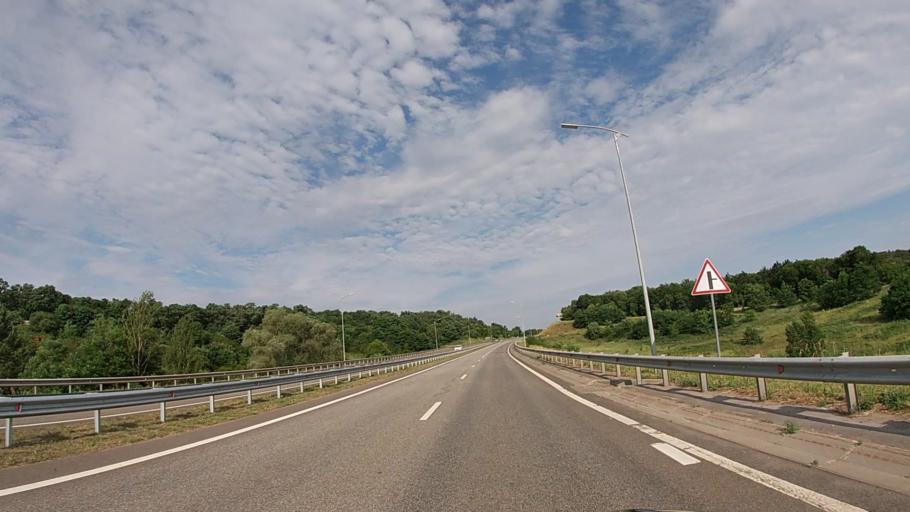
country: RU
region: Belgorod
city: Tomarovka
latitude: 50.6619
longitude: 36.3387
